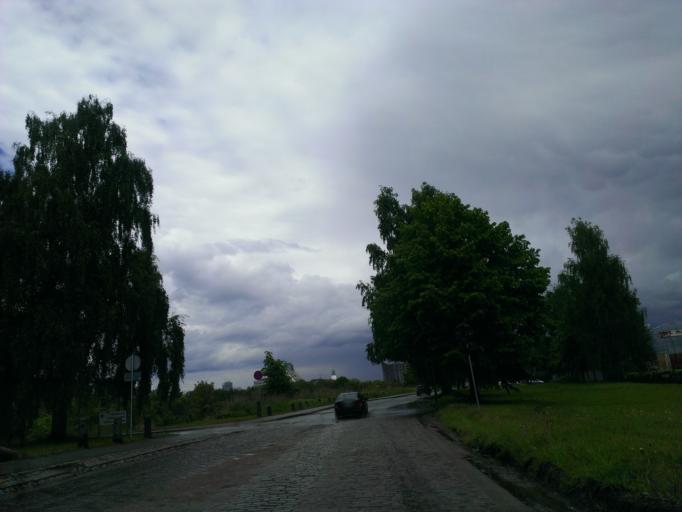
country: LV
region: Riga
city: Riga
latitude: 56.9312
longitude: 24.0919
